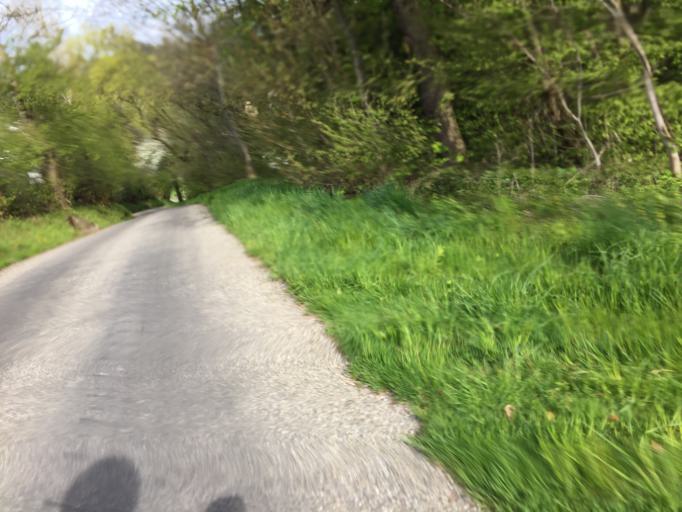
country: CH
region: Bern
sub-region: Bern-Mittelland District
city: Koniz
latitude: 46.9148
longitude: 7.3670
